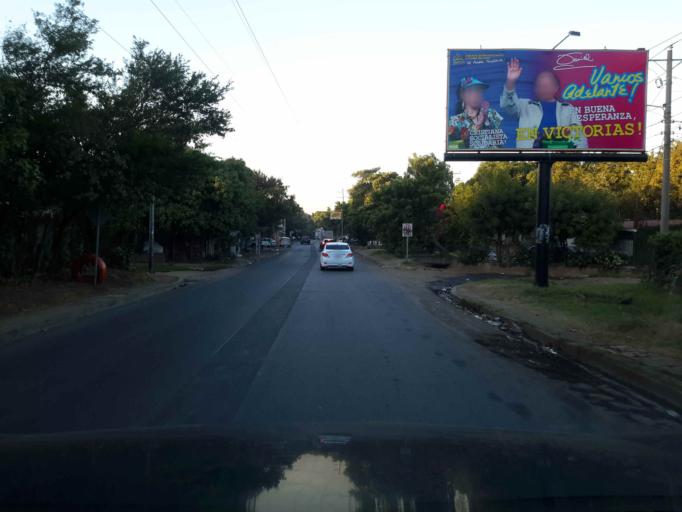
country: NI
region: Managua
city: Managua
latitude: 12.1086
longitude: -86.2336
